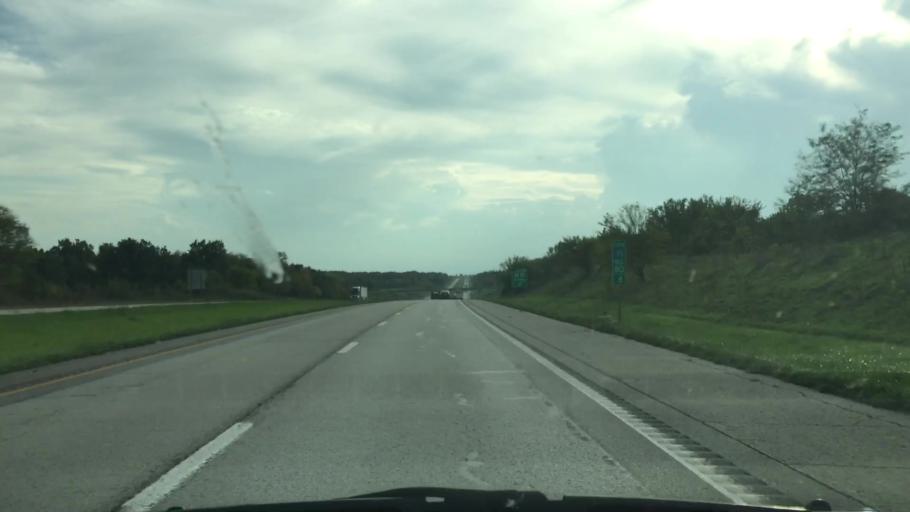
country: US
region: Missouri
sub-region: Harrison County
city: Bethany
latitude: 40.1103
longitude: -94.0665
